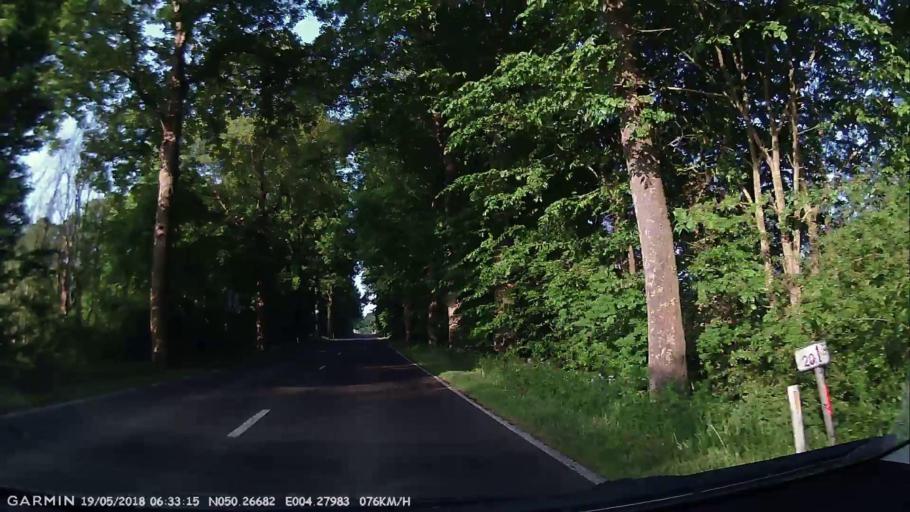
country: BE
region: Wallonia
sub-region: Province du Hainaut
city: Beaumont
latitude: 50.2668
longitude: 4.2798
